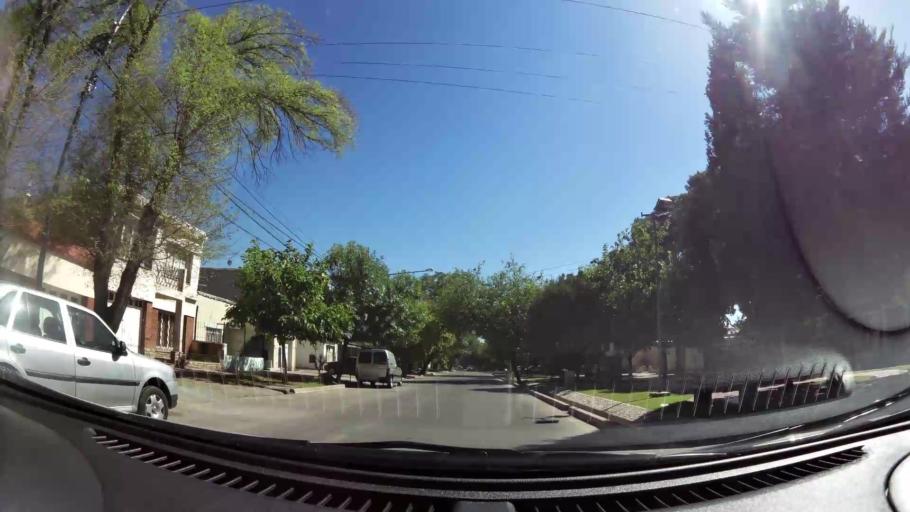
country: AR
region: Mendoza
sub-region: Departamento de Godoy Cruz
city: Godoy Cruz
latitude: -32.9056
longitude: -68.8562
